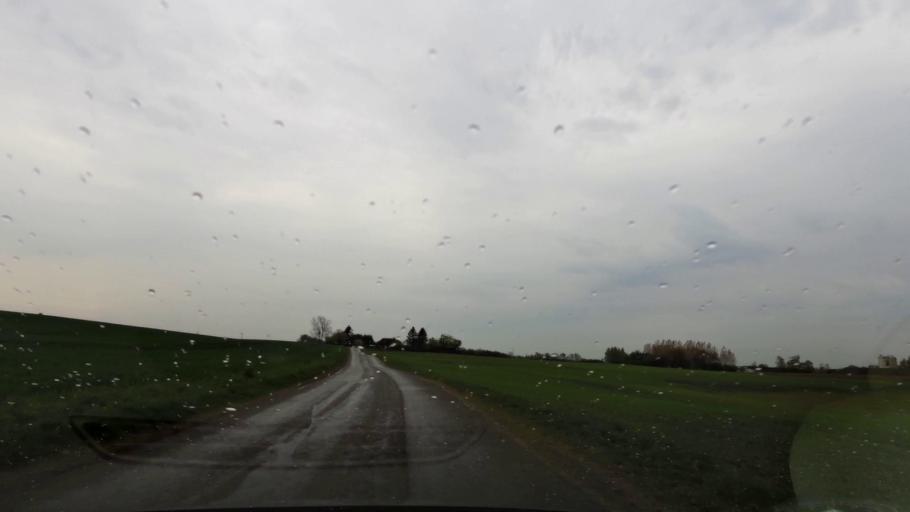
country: DK
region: South Denmark
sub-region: Svendborg Kommune
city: Svendborg
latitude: 55.1719
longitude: 10.5940
